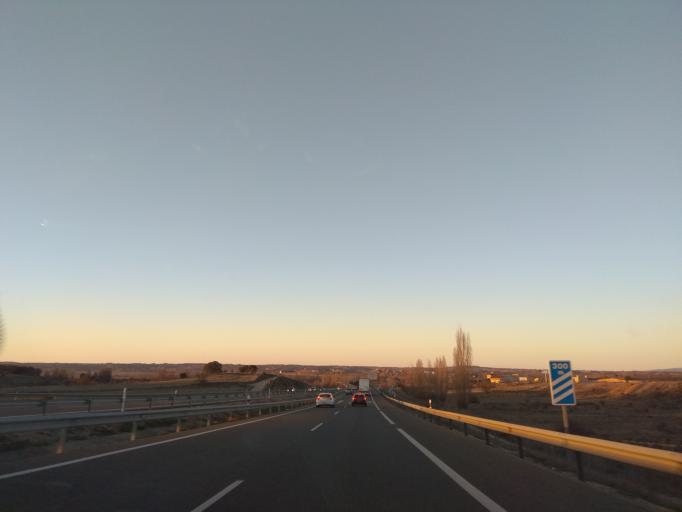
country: ES
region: Castille and Leon
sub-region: Provincia de Burgos
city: Villanueva de Gumiel
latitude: 41.7463
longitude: -3.6892
